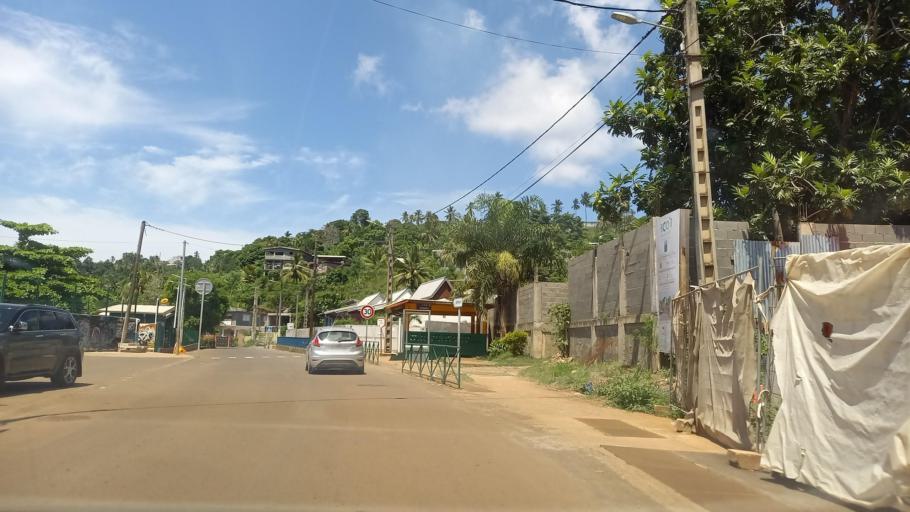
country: YT
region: M'Tsangamouji
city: M'Tsangamouji
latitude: -12.7608
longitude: 45.0854
